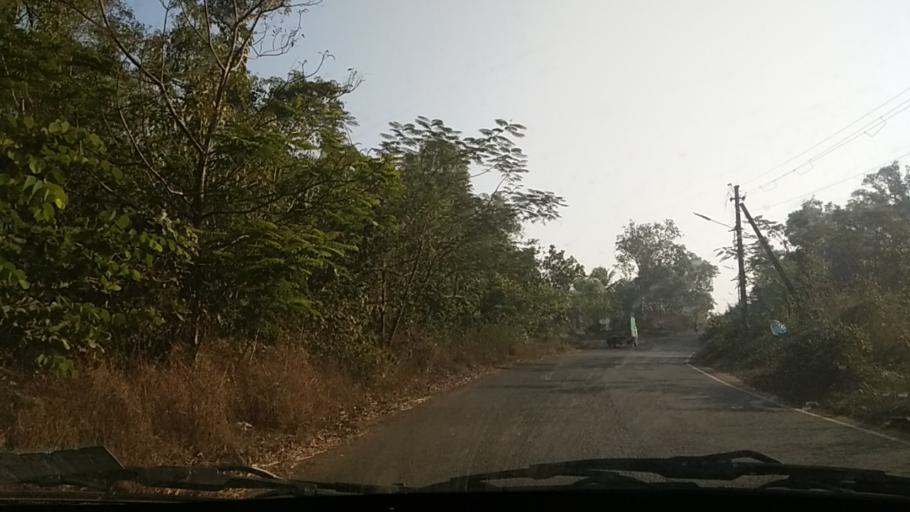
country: IN
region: Goa
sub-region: South Goa
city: Quepem
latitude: 15.1926
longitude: 74.0438
